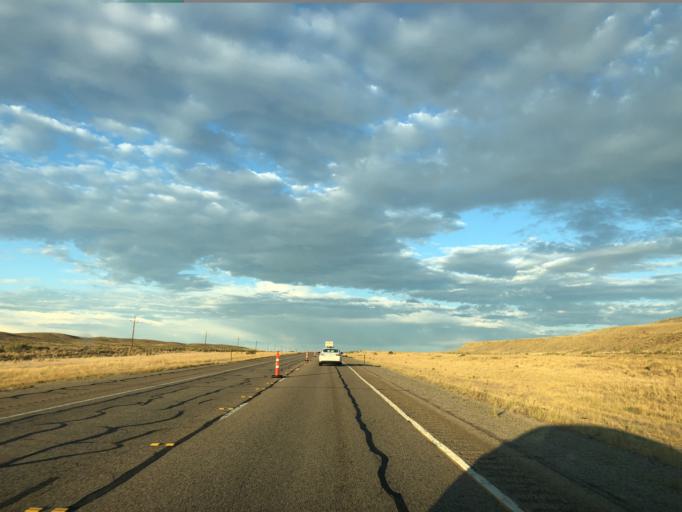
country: US
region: Wyoming
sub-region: Carbon County
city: Saratoga
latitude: 41.7438
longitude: -106.8926
